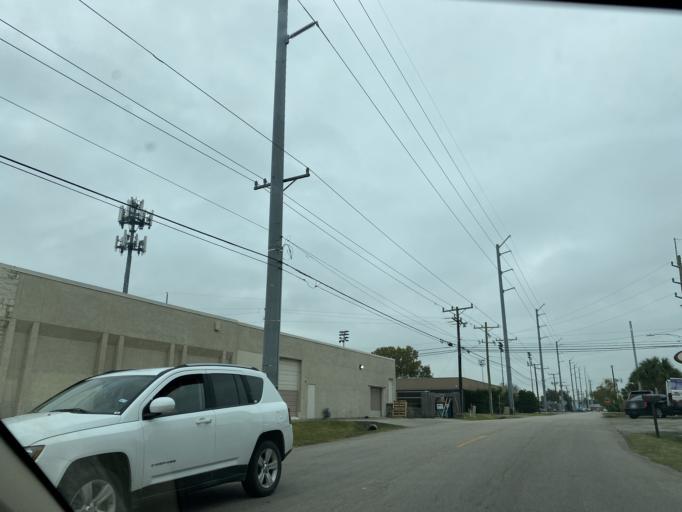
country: US
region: Texas
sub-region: Harris County
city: Bellaire
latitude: 29.7314
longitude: -95.4804
